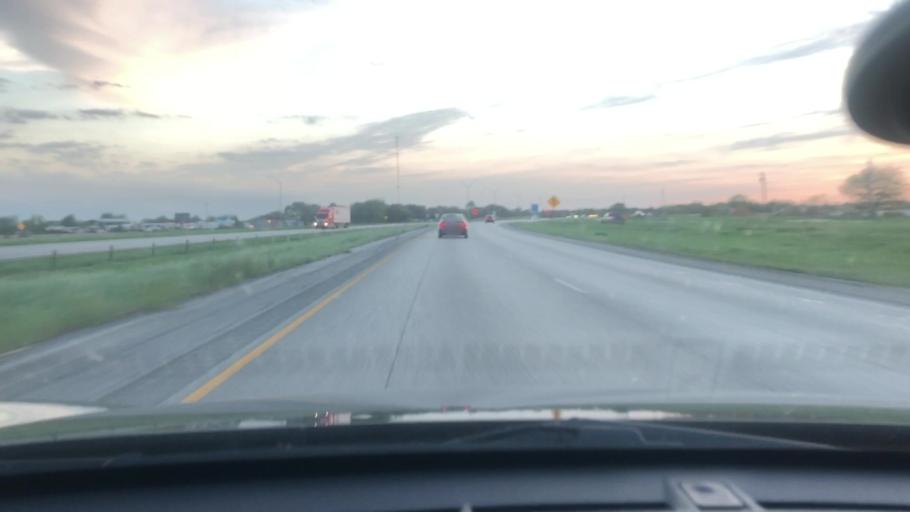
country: US
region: Texas
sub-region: Jackson County
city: Edna
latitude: 28.9664
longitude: -96.6730
